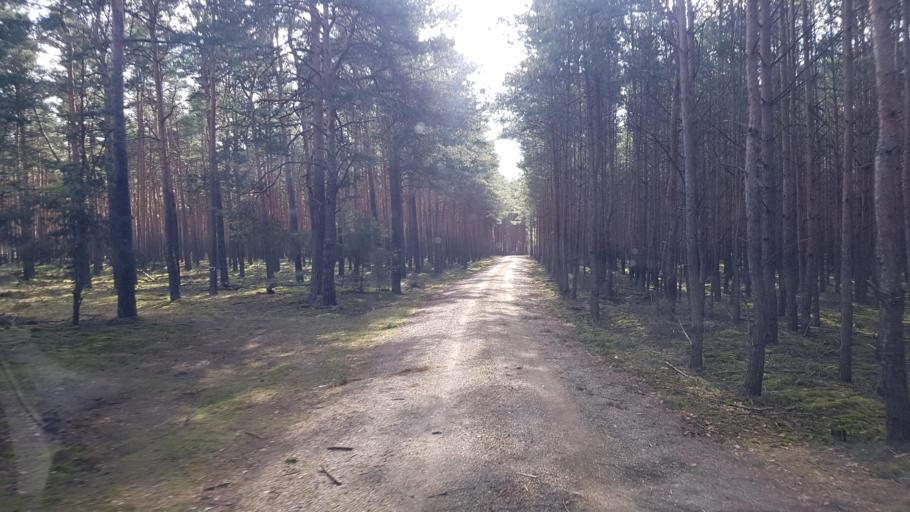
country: DE
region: Brandenburg
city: Schlieben
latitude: 51.6871
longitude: 13.4021
